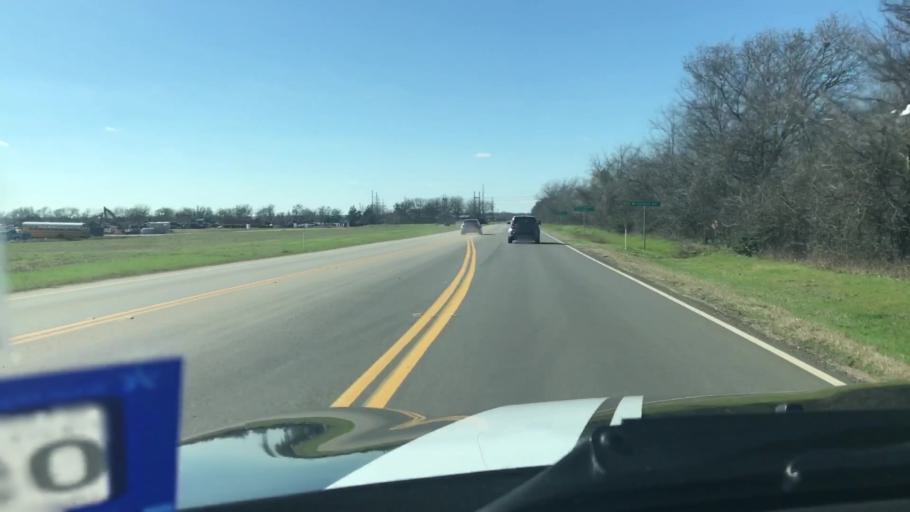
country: US
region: Texas
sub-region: Robertson County
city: Hearne
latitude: 30.8874
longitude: -96.6216
